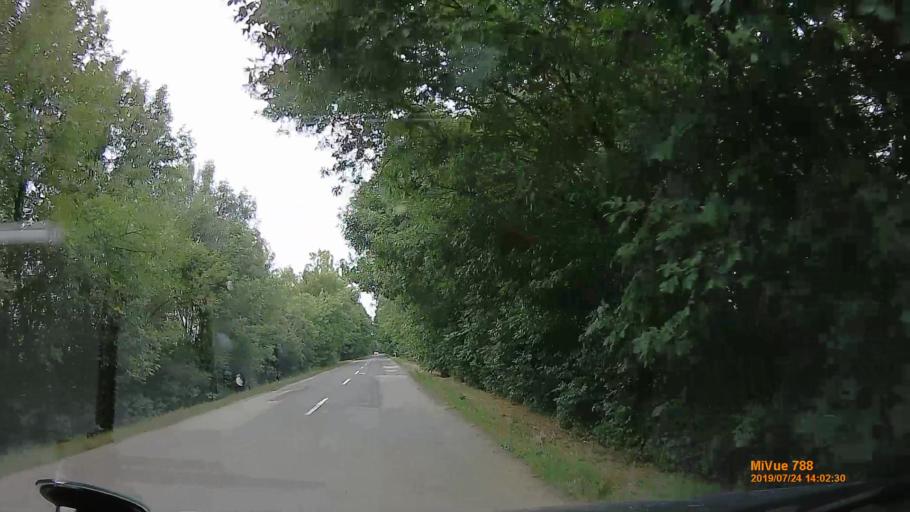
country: HU
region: Szabolcs-Szatmar-Bereg
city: Aranyosapati
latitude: 48.2681
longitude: 22.2872
